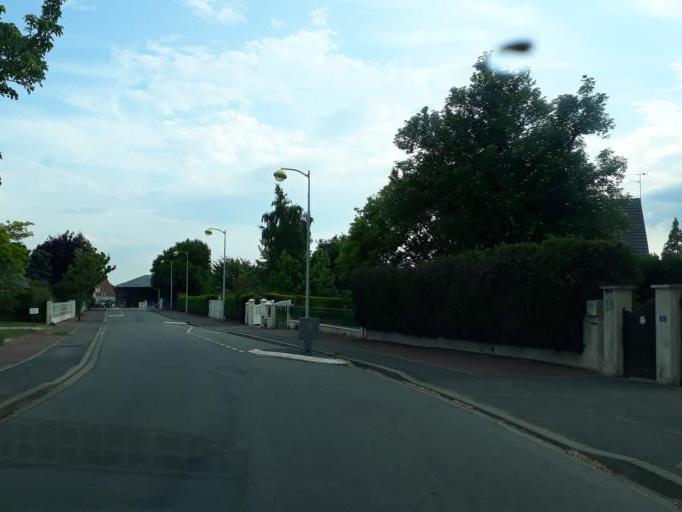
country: FR
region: Centre
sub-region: Departement du Loiret
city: Ormes
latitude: 47.9361
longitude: 1.8166
